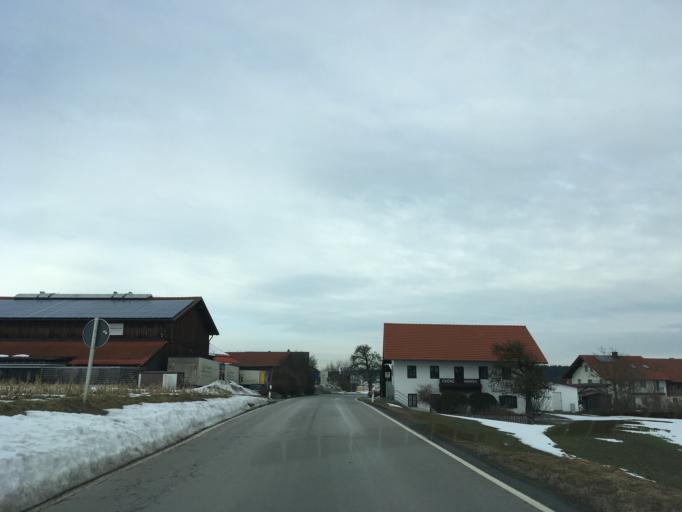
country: DE
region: Bavaria
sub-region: Upper Bavaria
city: Jettenbach
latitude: 48.1442
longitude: 12.3923
